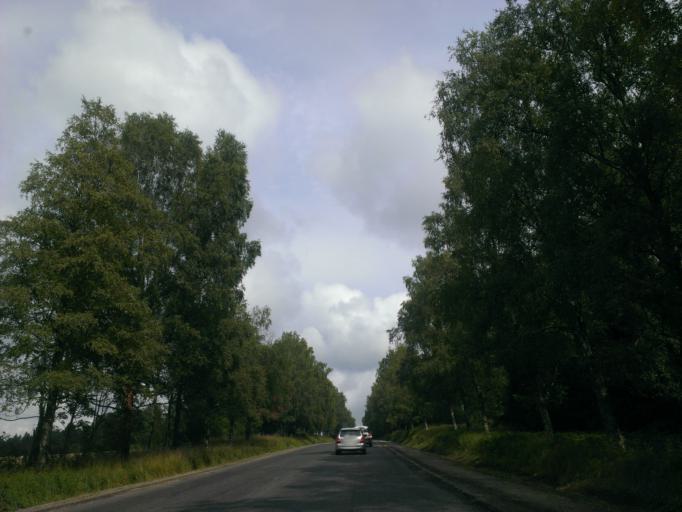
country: LV
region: Ligatne
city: Ligatne
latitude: 57.1954
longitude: 25.0945
